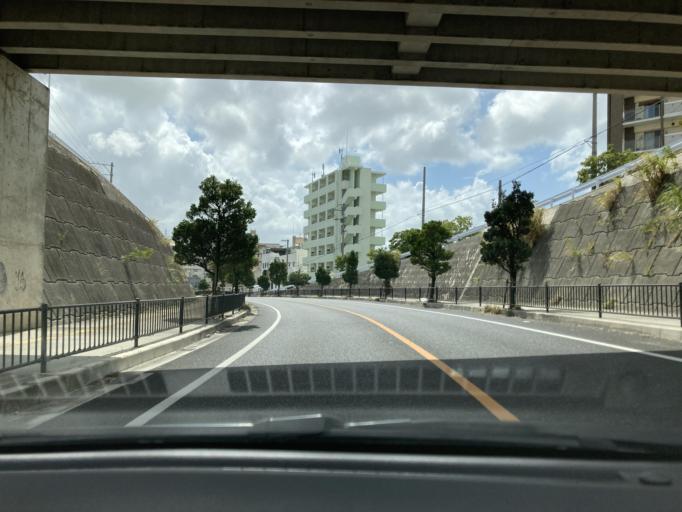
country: JP
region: Okinawa
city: Ginowan
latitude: 26.2635
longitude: 127.7302
